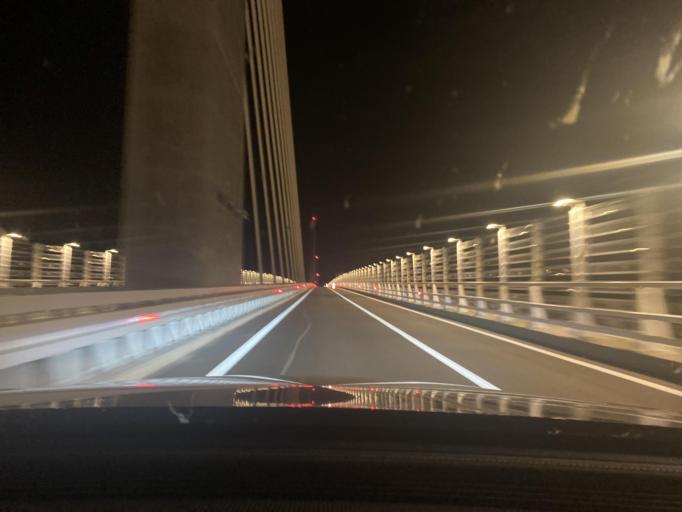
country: BA
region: Federation of Bosnia and Herzegovina
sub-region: Hercegovacko-Bosanski Kanton
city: Neum
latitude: 42.9351
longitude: 17.5392
